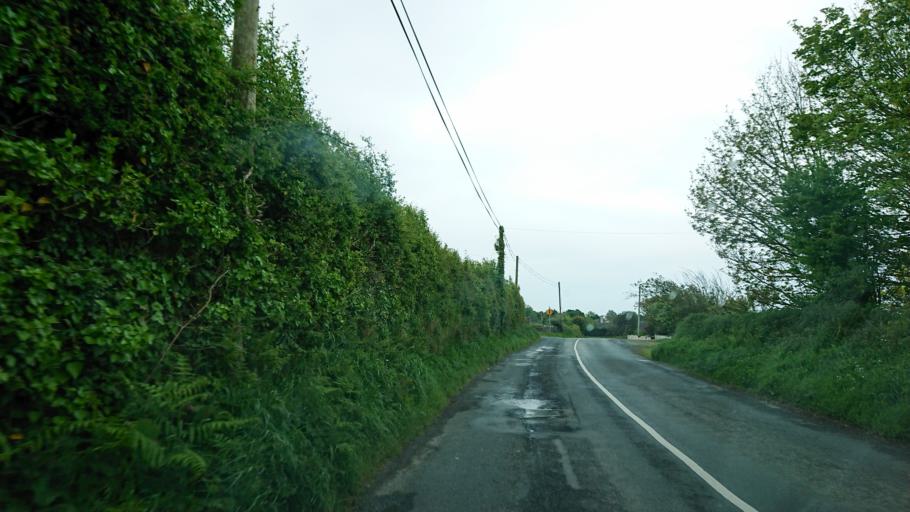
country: IE
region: Munster
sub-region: Waterford
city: Waterford
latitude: 52.2268
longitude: -7.0580
